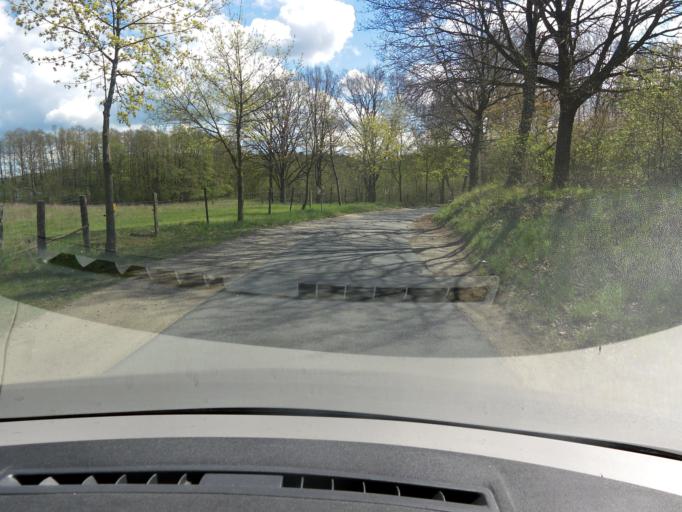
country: DE
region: Mecklenburg-Vorpommern
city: Malchow
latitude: 53.4632
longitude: 12.3568
